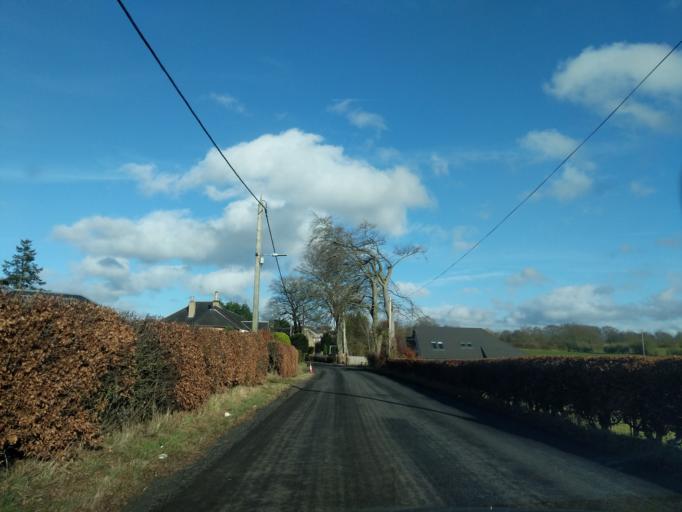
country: GB
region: Scotland
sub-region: South Lanarkshire
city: Carluke
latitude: 55.7225
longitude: -3.8348
